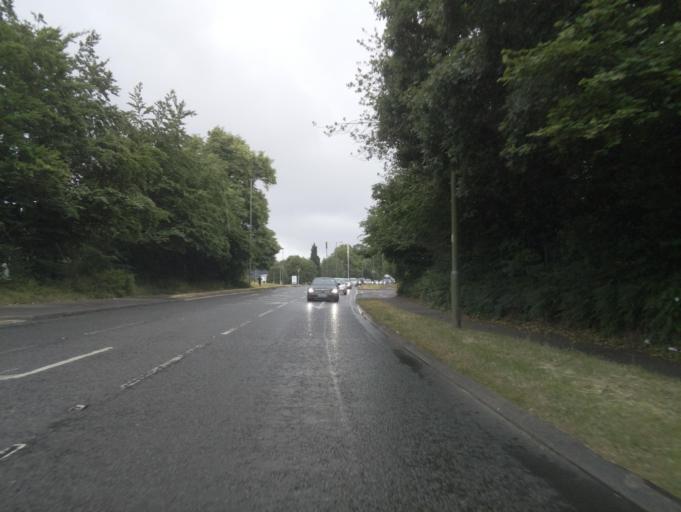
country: GB
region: England
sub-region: Surrey
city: Salfords
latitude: 51.1980
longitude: -0.1654
